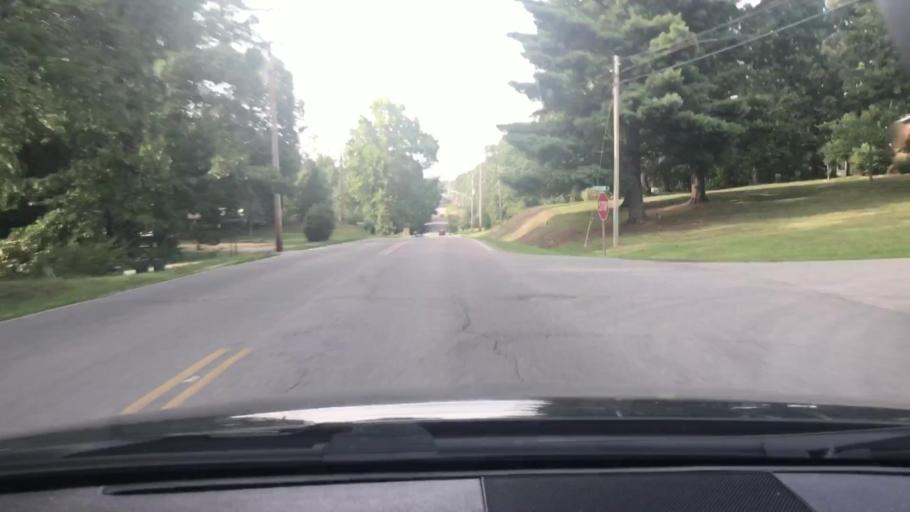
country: US
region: Tennessee
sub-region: Dickson County
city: White Bluff
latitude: 36.0955
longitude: -87.2139
